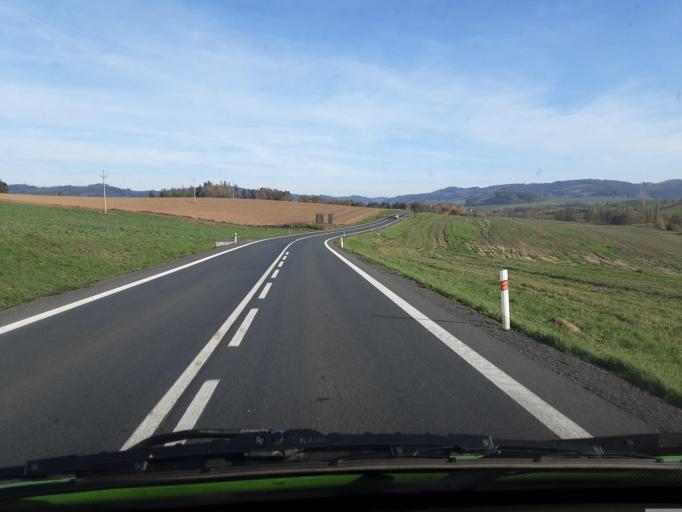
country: CZ
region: Plzensky
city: Klatovy
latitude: 49.3672
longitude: 13.3288
